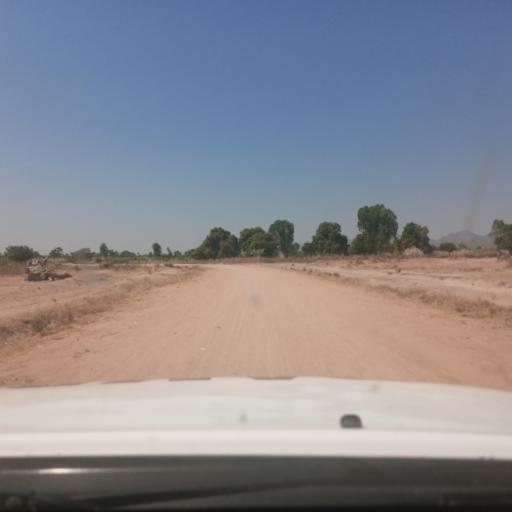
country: NG
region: Adamawa
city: Little Gombi
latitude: 9.7782
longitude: 12.5840
